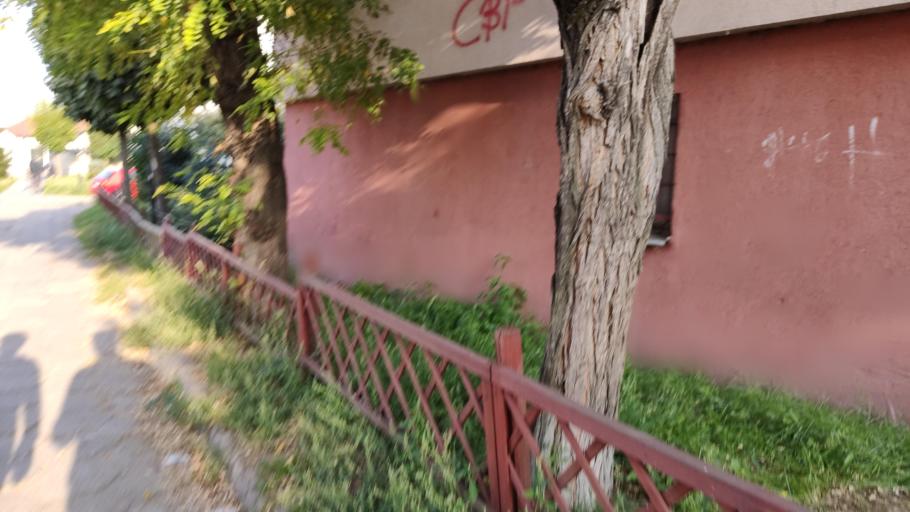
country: PL
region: Kujawsko-Pomorskie
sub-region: Powiat zninski
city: Znin
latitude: 52.8496
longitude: 17.7247
